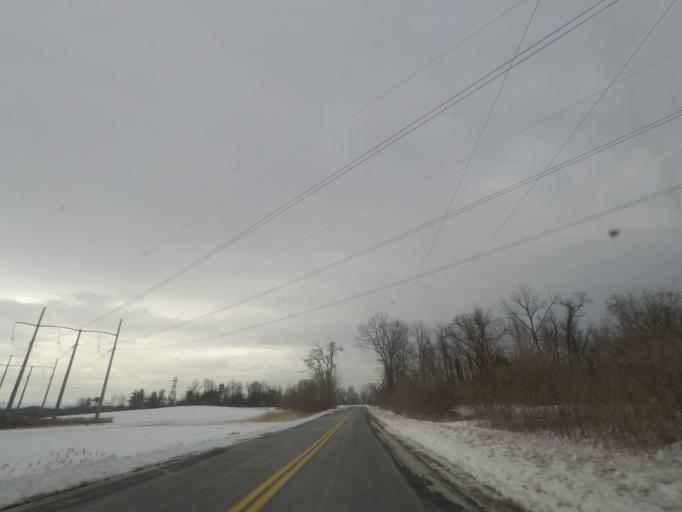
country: US
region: New York
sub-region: Rensselaer County
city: Castleton-on-Hudson
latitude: 42.4959
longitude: -73.7406
